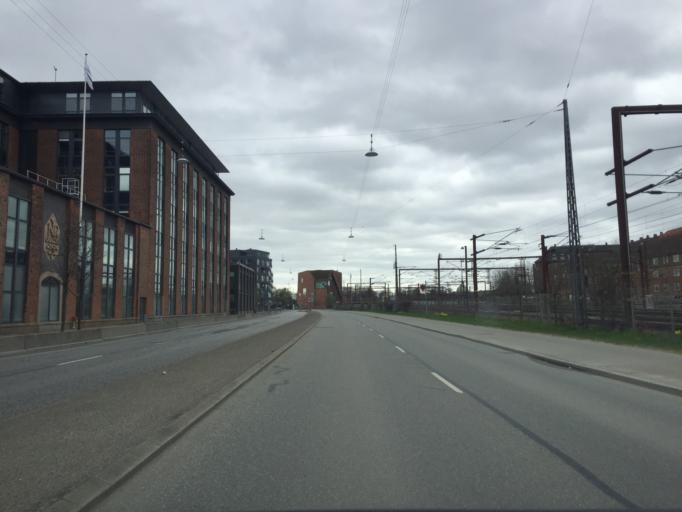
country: DK
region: Capital Region
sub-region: Kobenhavn
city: Christianshavn
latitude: 55.6994
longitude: 12.5926
